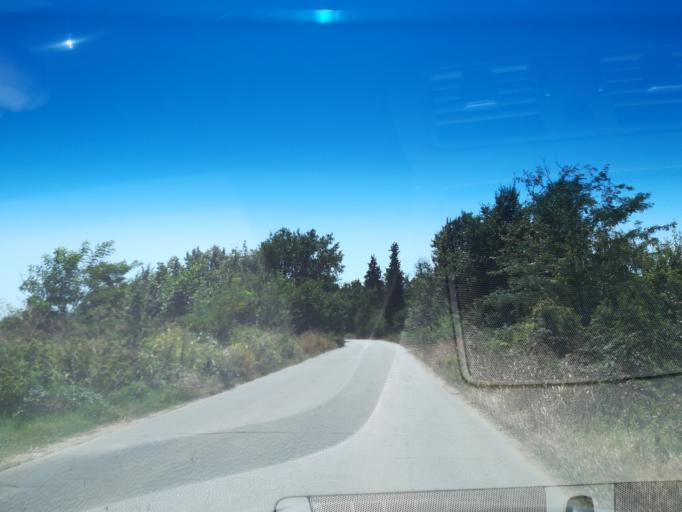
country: BG
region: Pazardzhik
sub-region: Obshtina Pazardzhik
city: Pazardzhik
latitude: 42.2874
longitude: 24.3950
